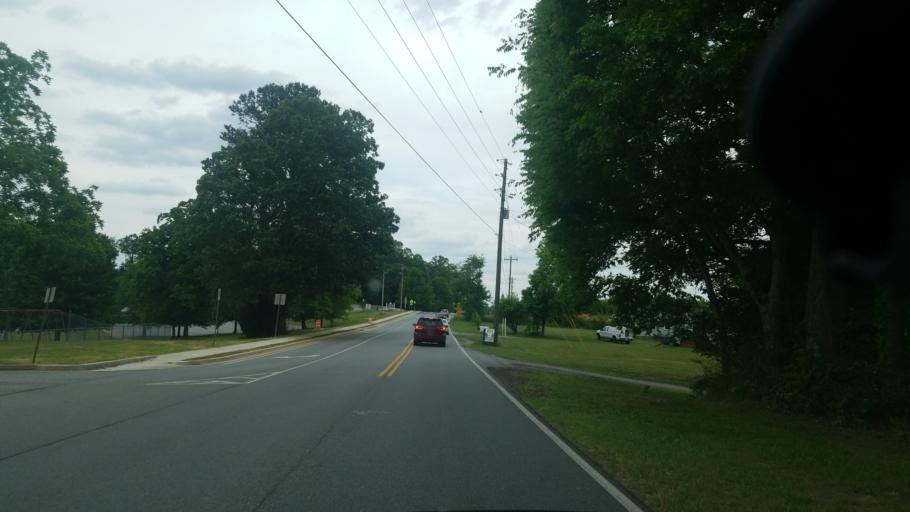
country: US
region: Georgia
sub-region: Forsyth County
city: Cumming
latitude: 34.1349
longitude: -84.1423
